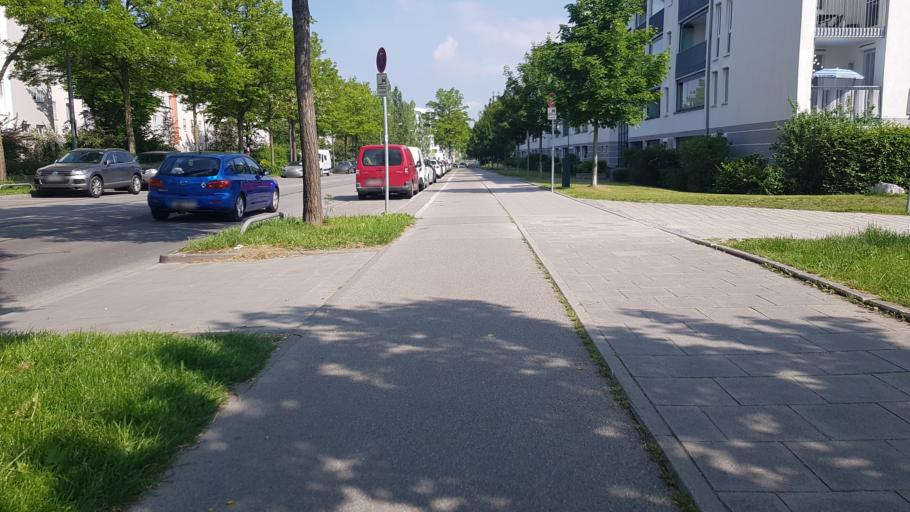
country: DE
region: Bavaria
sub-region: Upper Bavaria
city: Unterfoehring
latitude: 48.1652
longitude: 11.6448
